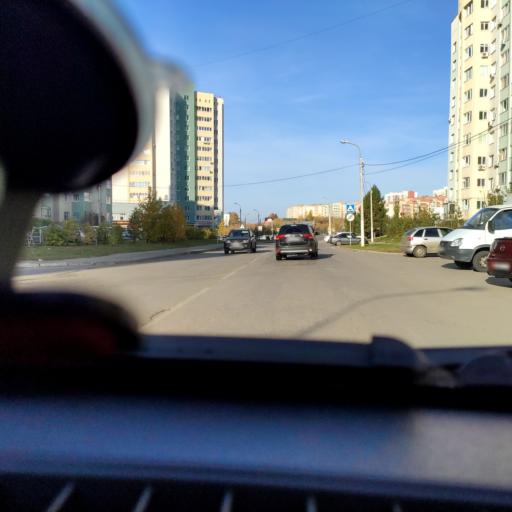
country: RU
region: Bashkortostan
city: Ufa
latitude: 54.6896
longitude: 55.9929
